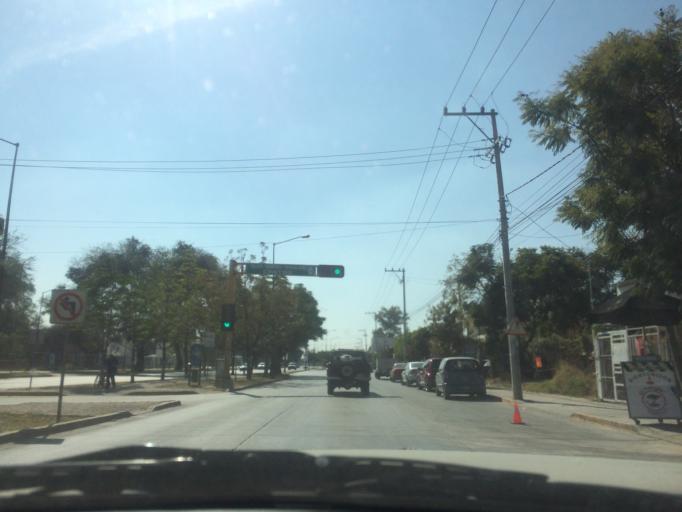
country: MX
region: Guanajuato
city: Leon
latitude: 21.1694
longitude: -101.6595
